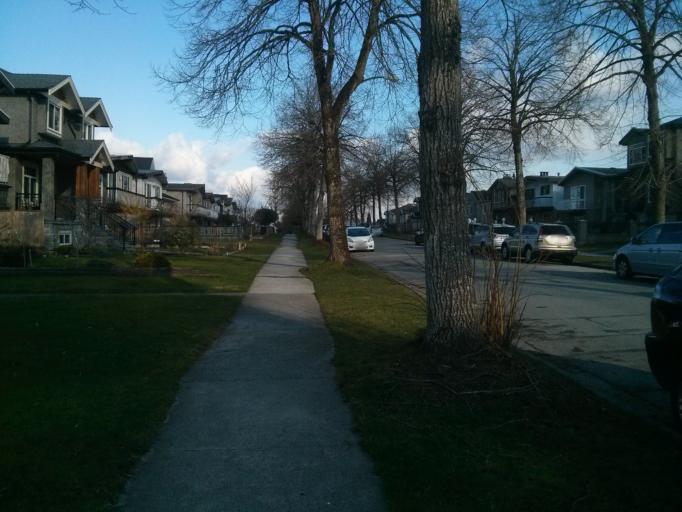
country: CA
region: British Columbia
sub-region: Fraser Valley Regional District
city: North Vancouver
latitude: 49.2454
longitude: -123.0331
